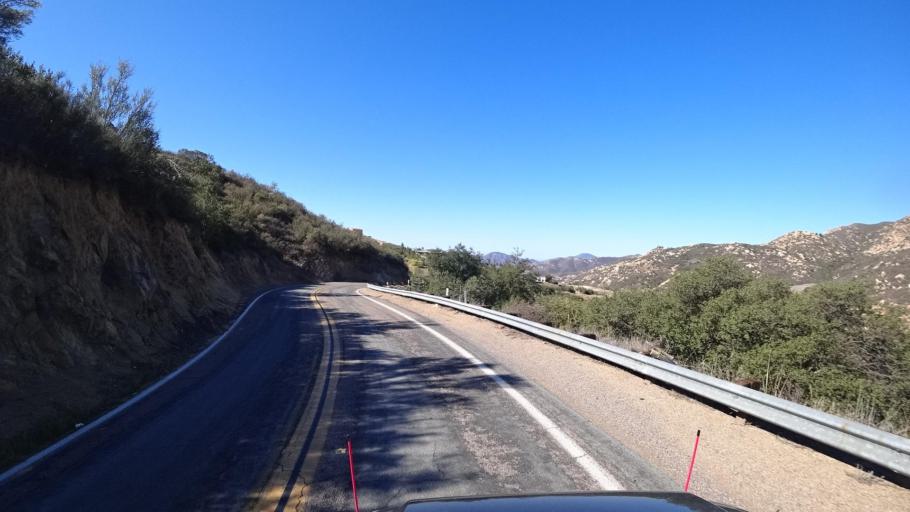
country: US
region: California
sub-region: San Diego County
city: Jamul
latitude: 32.7115
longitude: -116.7771
